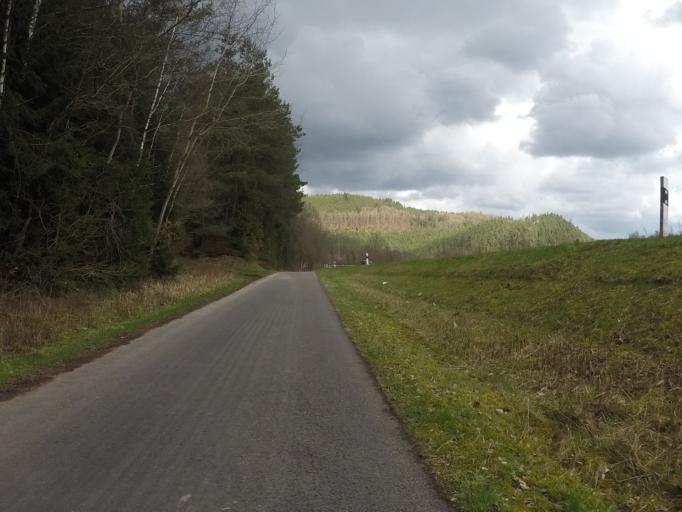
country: DE
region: Rheinland-Pfalz
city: Munchweiler an der Rodalbe
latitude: 49.2273
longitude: 7.6918
